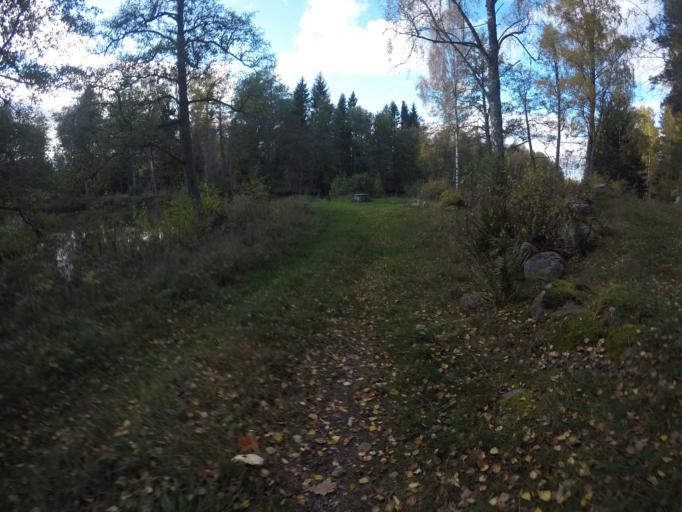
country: SE
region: Vaestmanland
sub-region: Arboga Kommun
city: Tyringe
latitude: 59.3394
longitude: 15.9628
